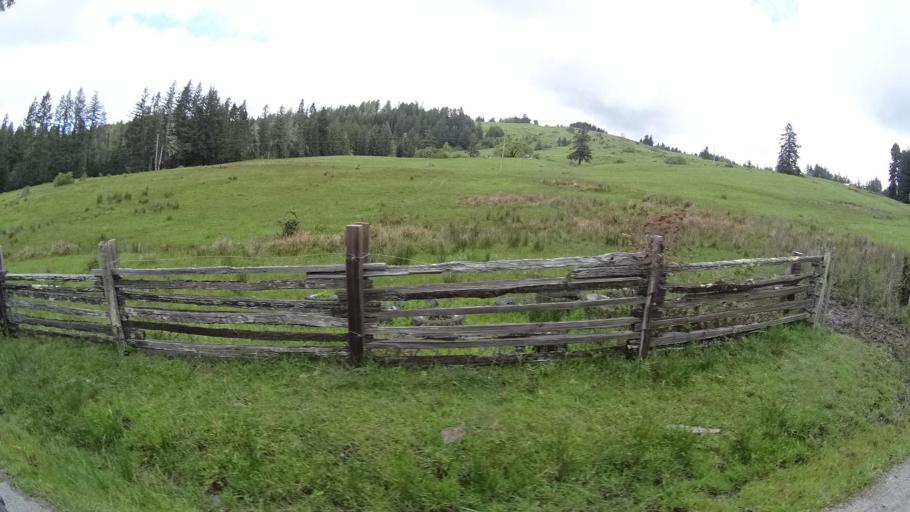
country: US
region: California
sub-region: Humboldt County
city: Blue Lake
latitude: 40.9086
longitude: -123.9687
